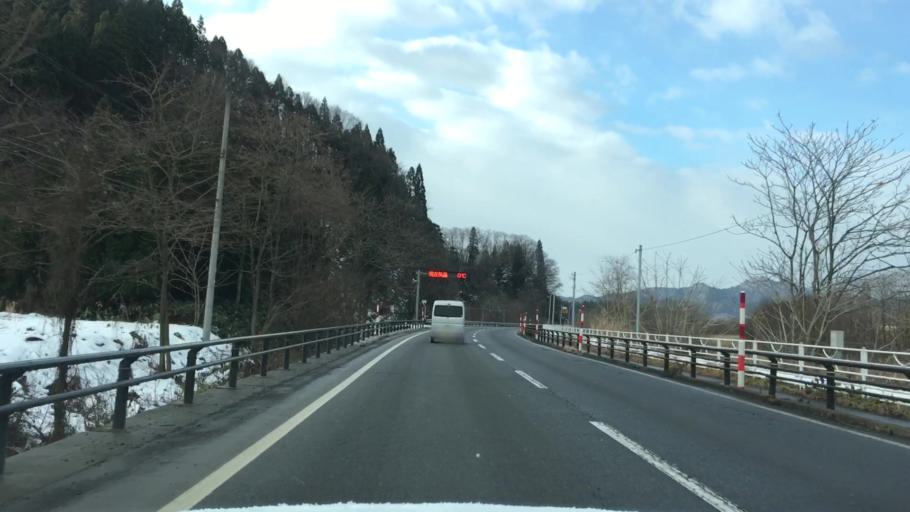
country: JP
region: Akita
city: Odate
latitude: 40.3353
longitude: 140.5869
